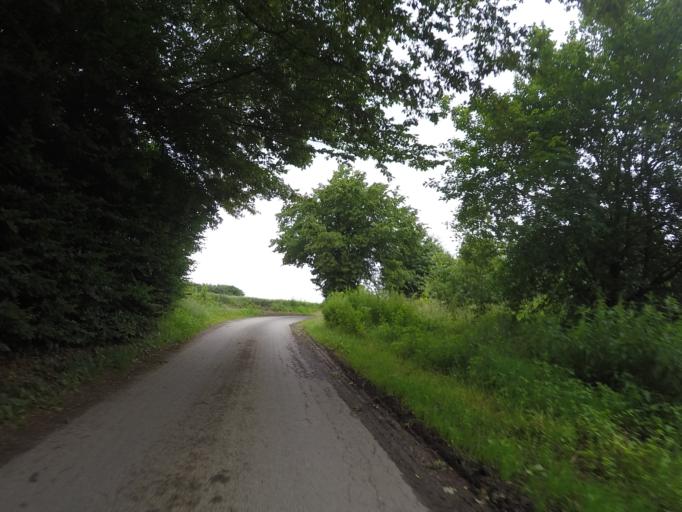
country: BE
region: Wallonia
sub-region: Province de Namur
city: Yvoir
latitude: 50.3261
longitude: 4.9104
